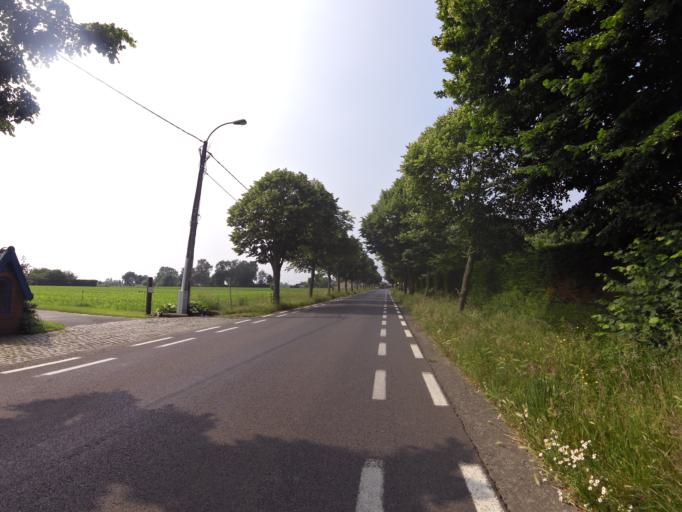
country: BE
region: Flanders
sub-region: Provincie West-Vlaanderen
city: Ichtegem
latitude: 51.1113
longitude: 3.0433
